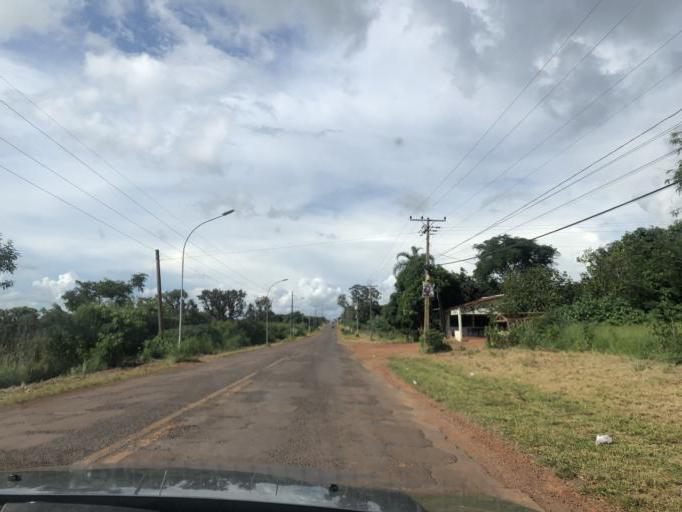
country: BR
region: Federal District
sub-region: Brasilia
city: Brasilia
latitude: -15.7438
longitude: -48.1256
